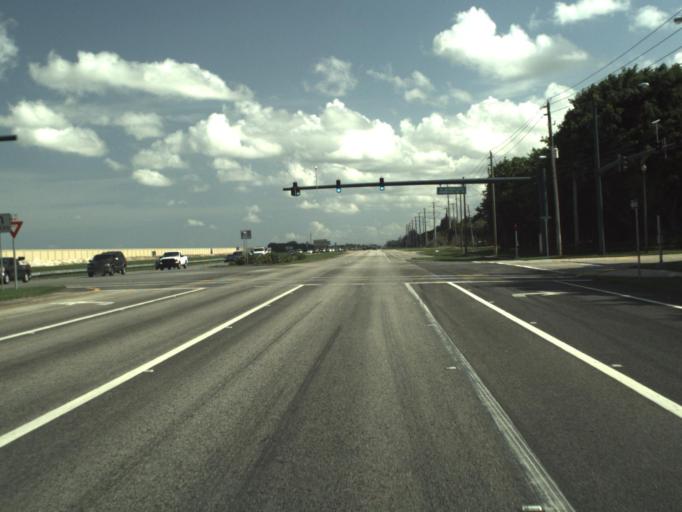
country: US
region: Florida
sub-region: Palm Beach County
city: Villages of Oriole
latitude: 26.4384
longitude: -80.2046
